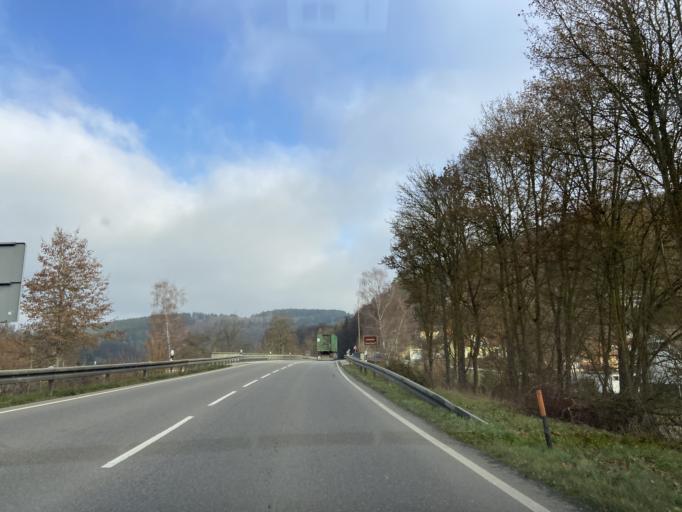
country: DE
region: Baden-Wuerttemberg
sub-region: Tuebingen Region
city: Veringenstadt
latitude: 48.1816
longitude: 9.2125
